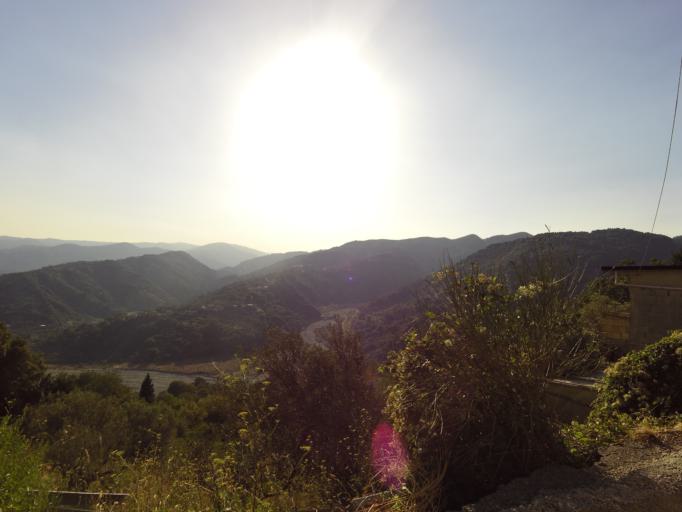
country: IT
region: Calabria
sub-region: Provincia di Reggio Calabria
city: Pazzano
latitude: 38.4493
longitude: 16.4130
